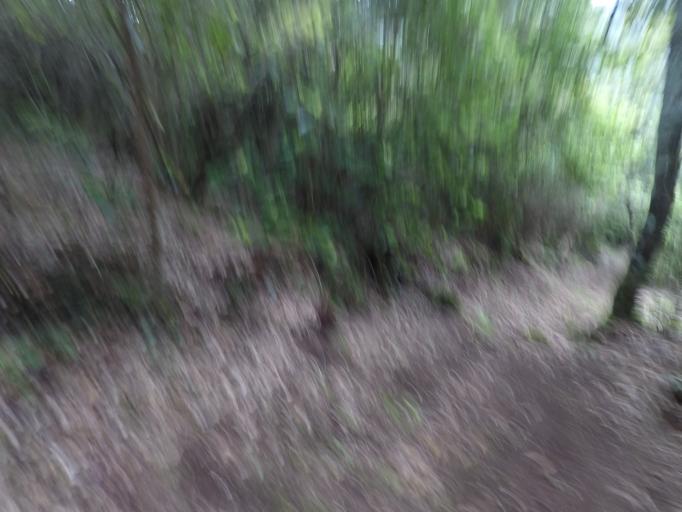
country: PT
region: Madeira
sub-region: Camara de Lobos
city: Curral das Freiras
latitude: 32.7751
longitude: -16.9806
